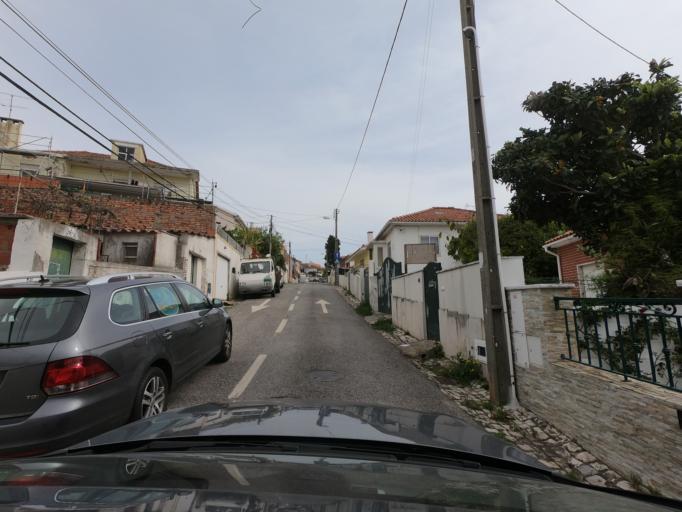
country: PT
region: Lisbon
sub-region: Oeiras
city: Porto Salvo
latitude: 38.7182
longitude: -9.2913
